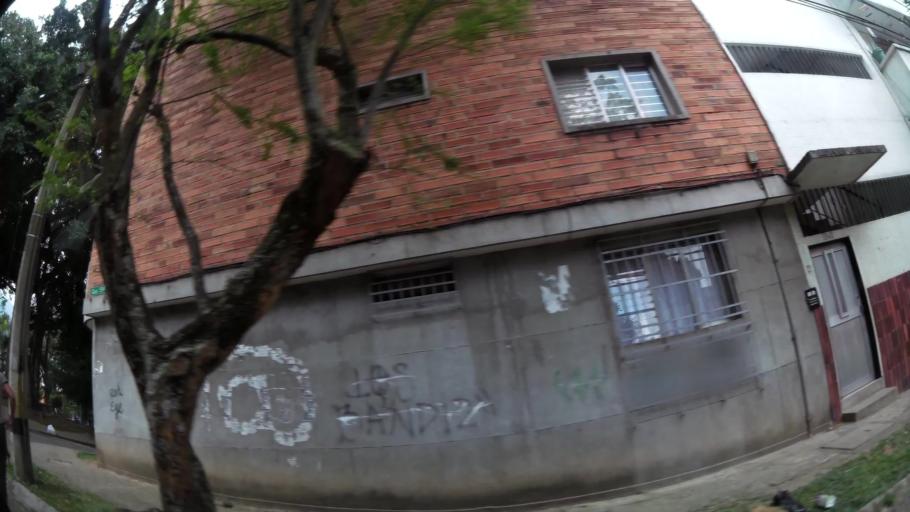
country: CO
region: Antioquia
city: Medellin
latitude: 6.2519
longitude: -75.5567
